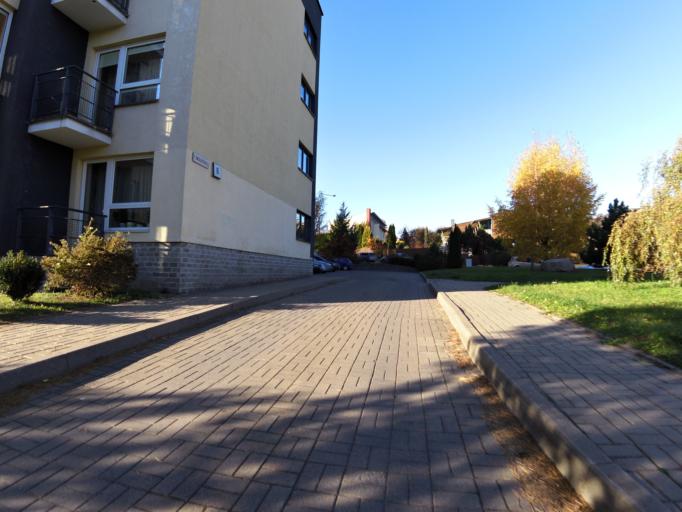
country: LT
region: Vilnius County
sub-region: Vilnius
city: Fabijoniskes
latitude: 54.7362
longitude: 25.2766
